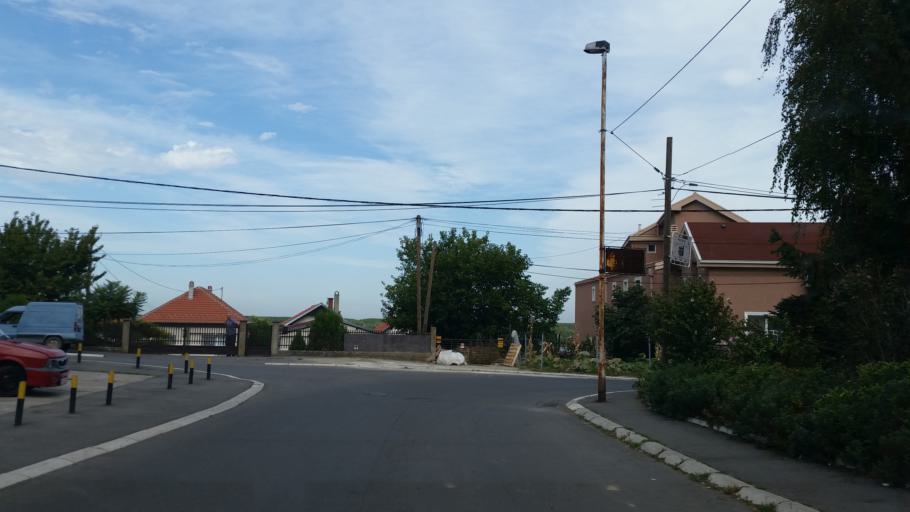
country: RS
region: Central Serbia
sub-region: Belgrade
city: Palilula
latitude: 44.8291
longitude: 20.5488
